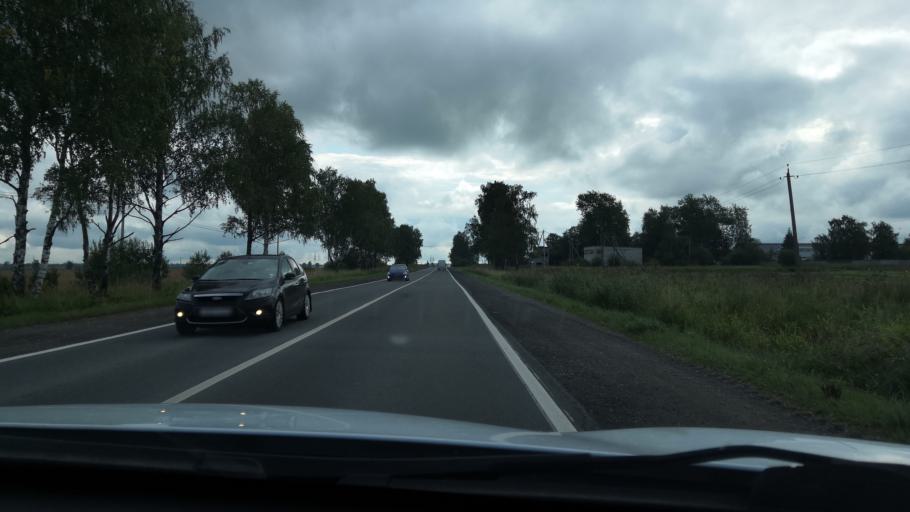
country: RU
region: St.-Petersburg
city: Tyarlevo
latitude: 59.7096
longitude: 30.4939
